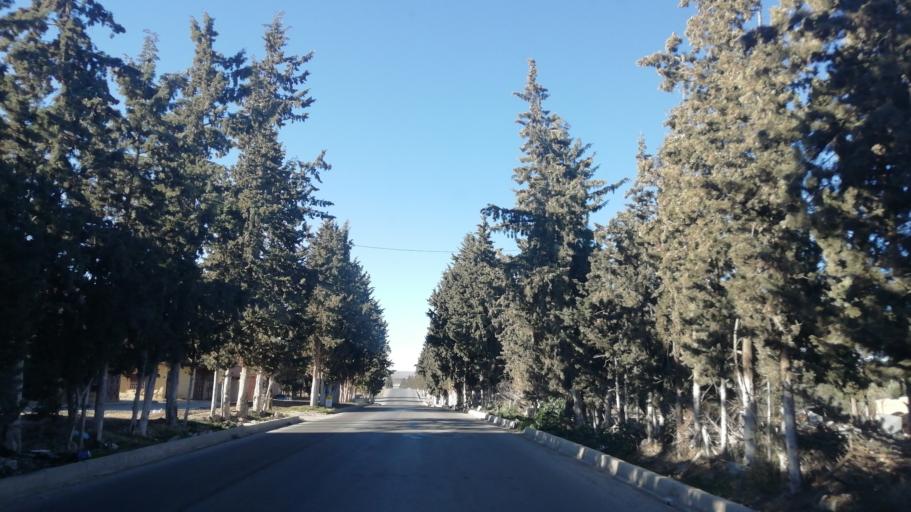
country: DZ
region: Saida
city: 'Ain el Hadjar
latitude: 34.7669
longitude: 0.1375
